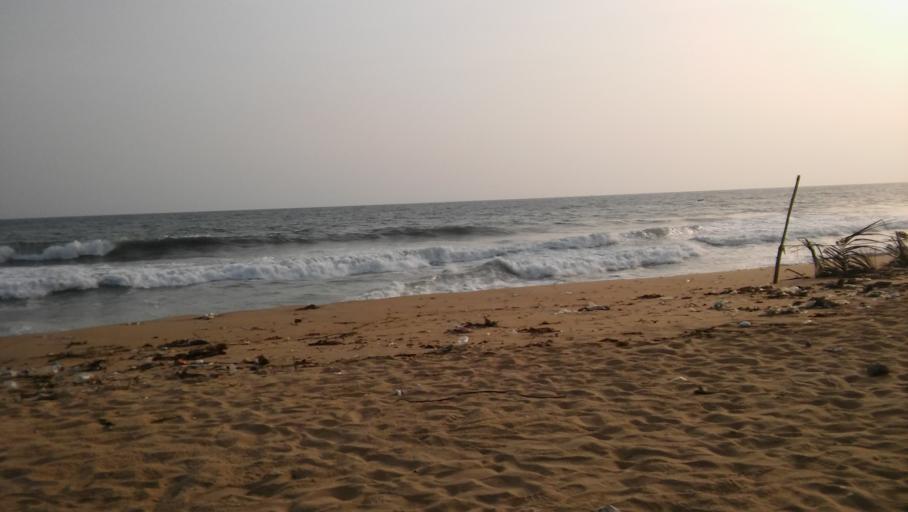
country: CI
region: Sud-Comoe
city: Grand-Bassam
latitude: 5.1919
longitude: -3.7247
